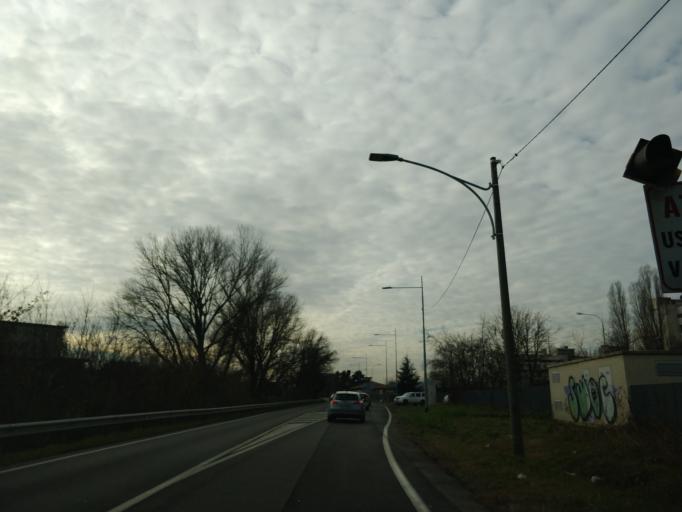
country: IT
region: Emilia-Romagna
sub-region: Provincia di Bologna
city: Progresso
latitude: 44.5367
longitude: 11.3692
